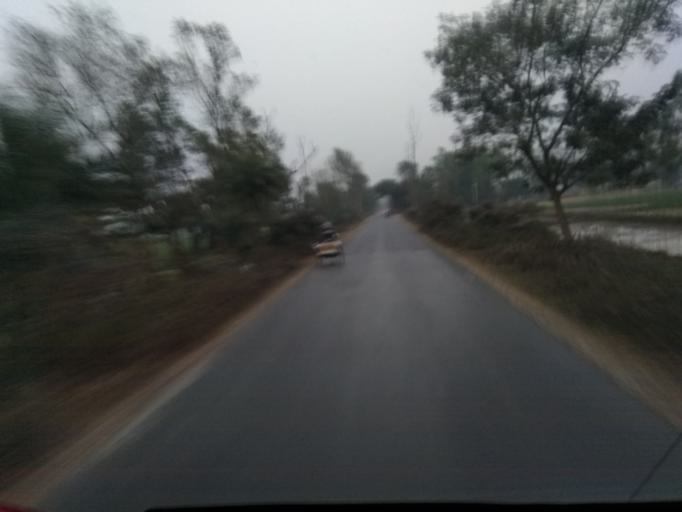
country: BD
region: Rajshahi
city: Bogra
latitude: 24.7454
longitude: 89.3377
